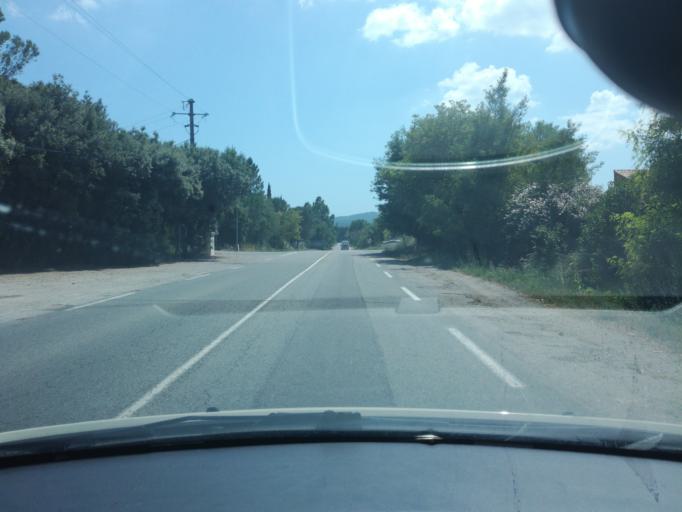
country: FR
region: Provence-Alpes-Cote d'Azur
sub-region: Departement du Var
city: Le Muy
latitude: 43.4852
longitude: 6.5672
